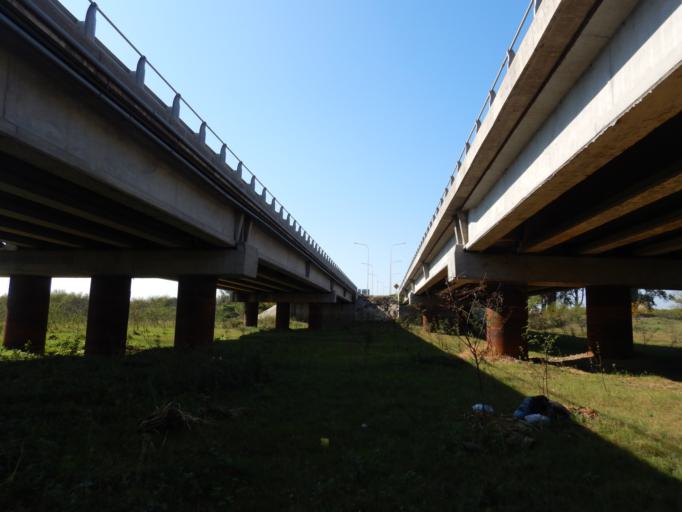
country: AR
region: Entre Rios
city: Parana
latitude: -31.6688
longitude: -60.5825
